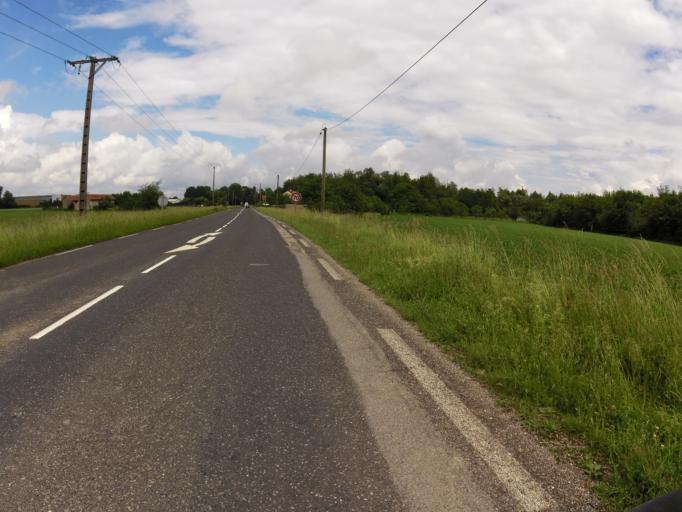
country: FR
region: Lorraine
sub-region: Departement de la Meuse
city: Revigny-sur-Ornain
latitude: 48.8141
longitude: 4.9735
